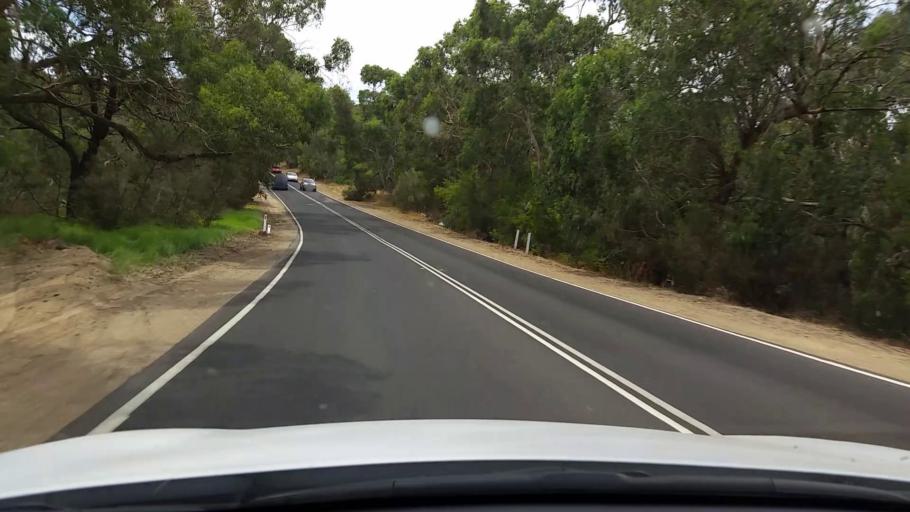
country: AU
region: Victoria
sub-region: Mornington Peninsula
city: Safety Beach
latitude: -38.3050
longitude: 145.0397
